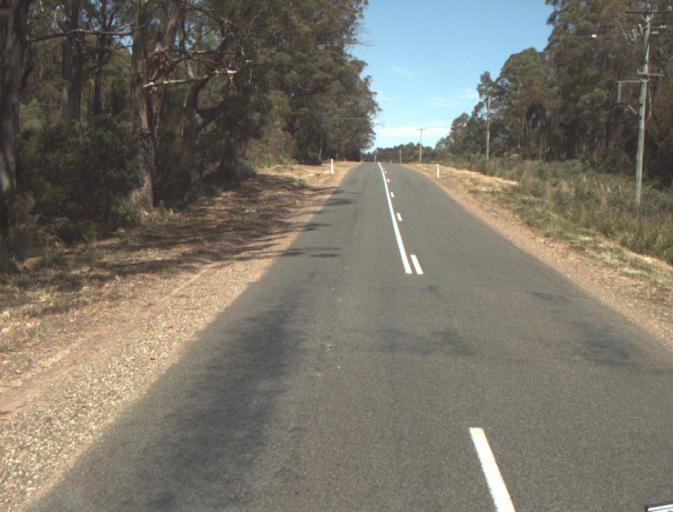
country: AU
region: Tasmania
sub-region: Launceston
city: Mayfield
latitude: -41.3059
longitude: 147.1337
